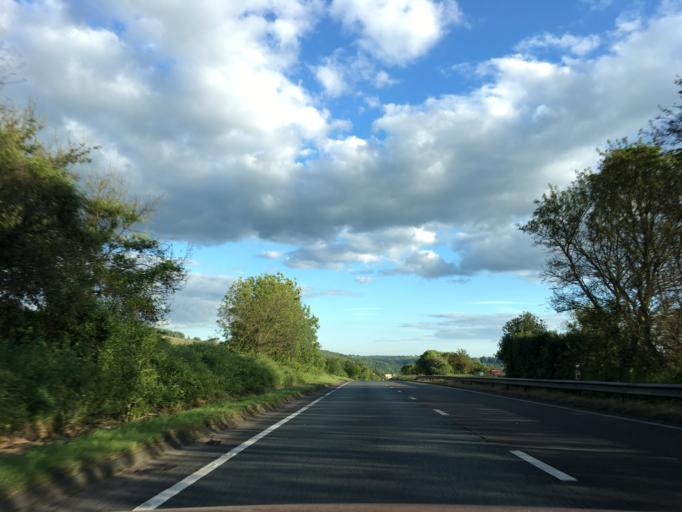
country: GB
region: England
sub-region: Herefordshire
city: Marstow
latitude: 51.8770
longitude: -2.6304
